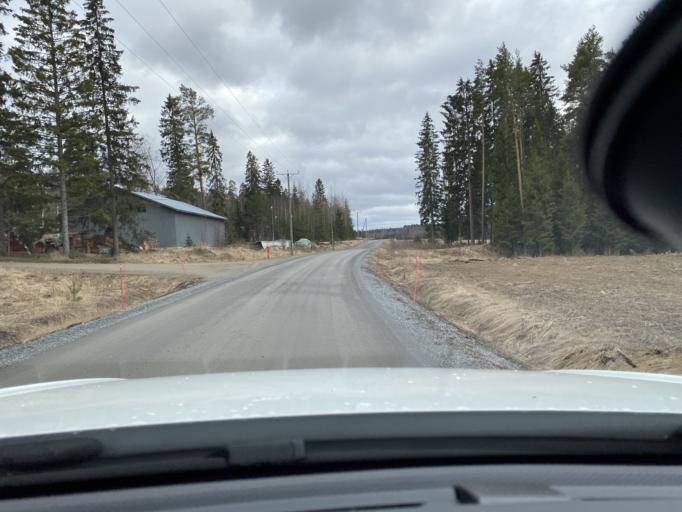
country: FI
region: Pirkanmaa
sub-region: Lounais-Pirkanmaa
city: Punkalaidun
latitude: 61.0934
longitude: 23.2291
